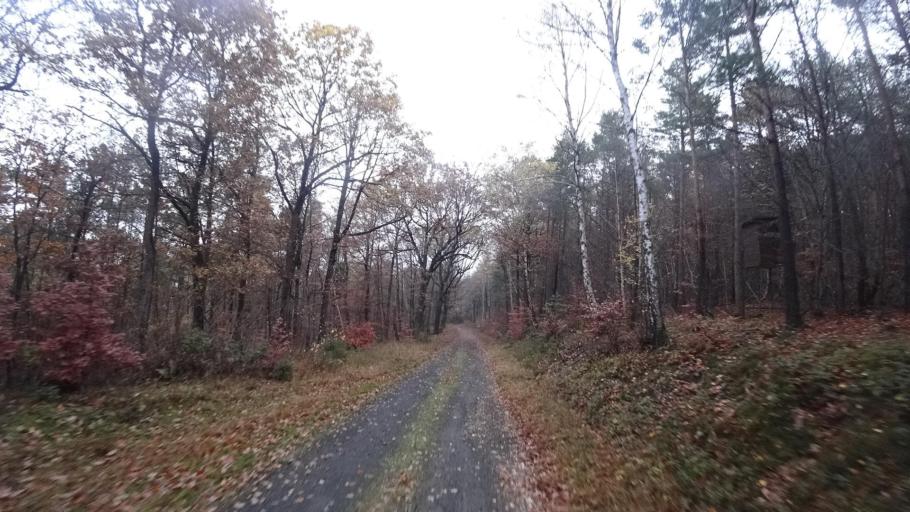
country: DE
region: Rheinland-Pfalz
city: Schalkenbach
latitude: 50.5200
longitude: 7.1300
